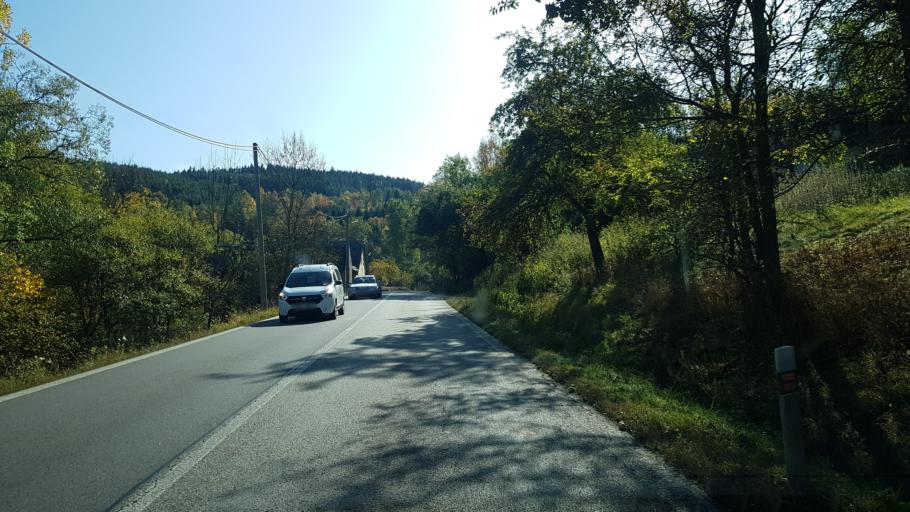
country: CZ
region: Jihocesky
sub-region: Okres Prachatice
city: Vimperk
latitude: 49.0891
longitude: 13.7939
